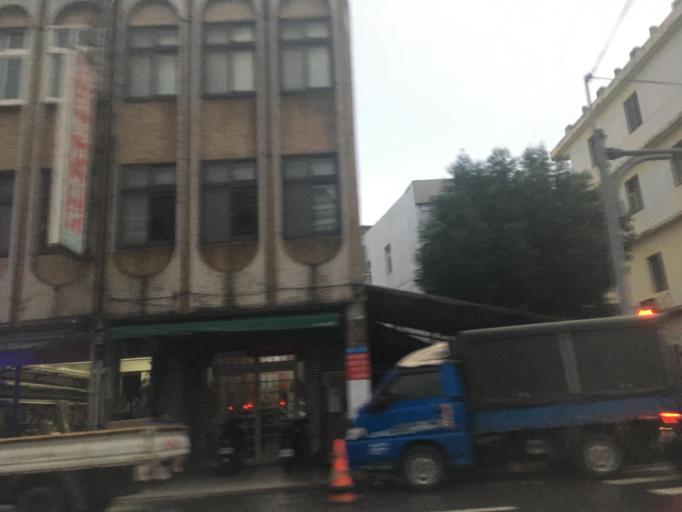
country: TW
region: Taiwan
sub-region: Yilan
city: Yilan
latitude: 24.8558
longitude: 121.8238
